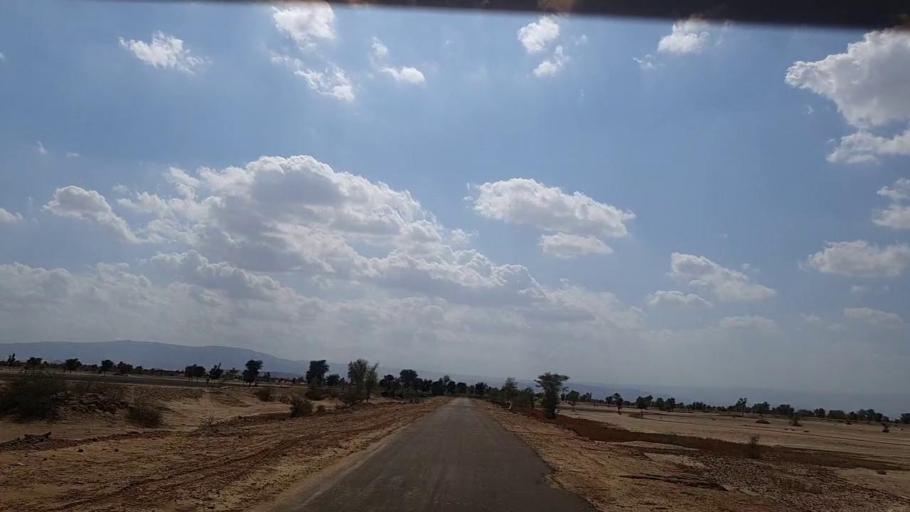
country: PK
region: Sindh
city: Johi
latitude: 26.5223
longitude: 67.4939
